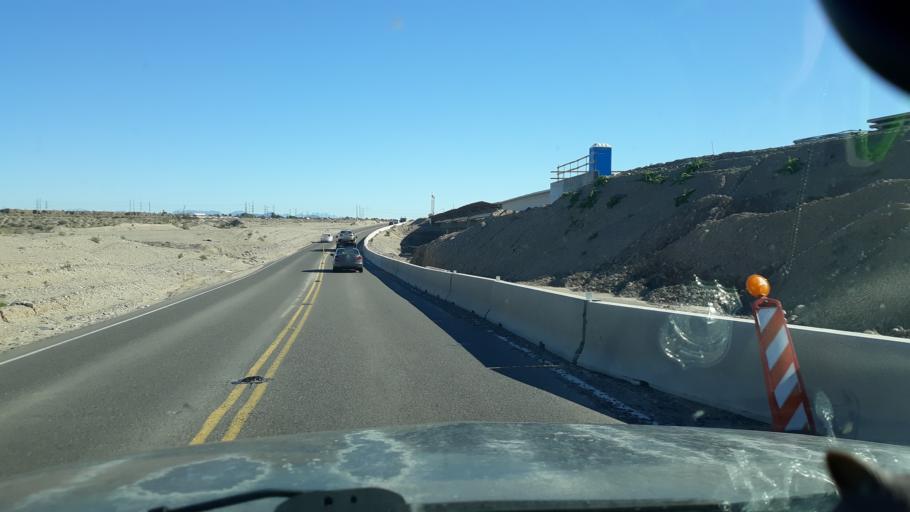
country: US
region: Arizona
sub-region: Maricopa County
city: Youngtown
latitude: 33.5513
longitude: -112.3184
